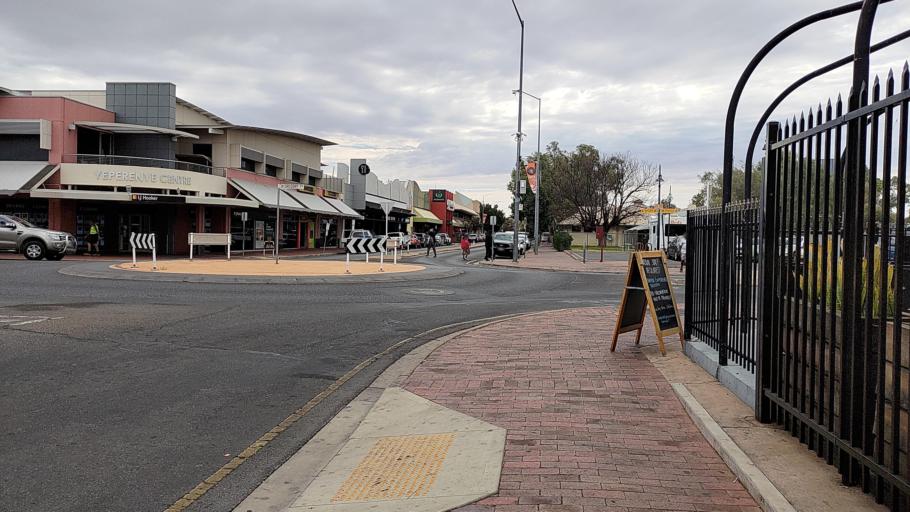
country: AU
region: Northern Territory
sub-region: Alice Springs
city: Alice Springs
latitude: -23.7005
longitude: 133.8808
